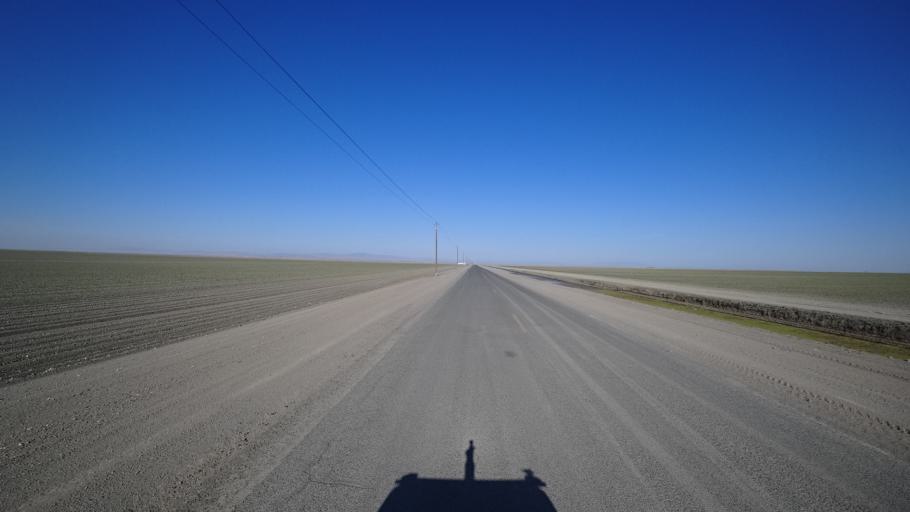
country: US
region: California
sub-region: Kings County
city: Stratford
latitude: 36.0796
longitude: -119.7809
